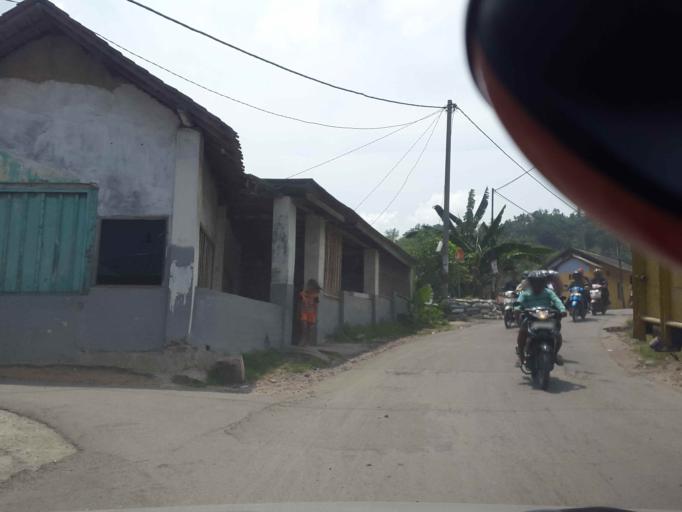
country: ID
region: Lampung
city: Panjang
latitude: -5.4627
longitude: 105.3216
